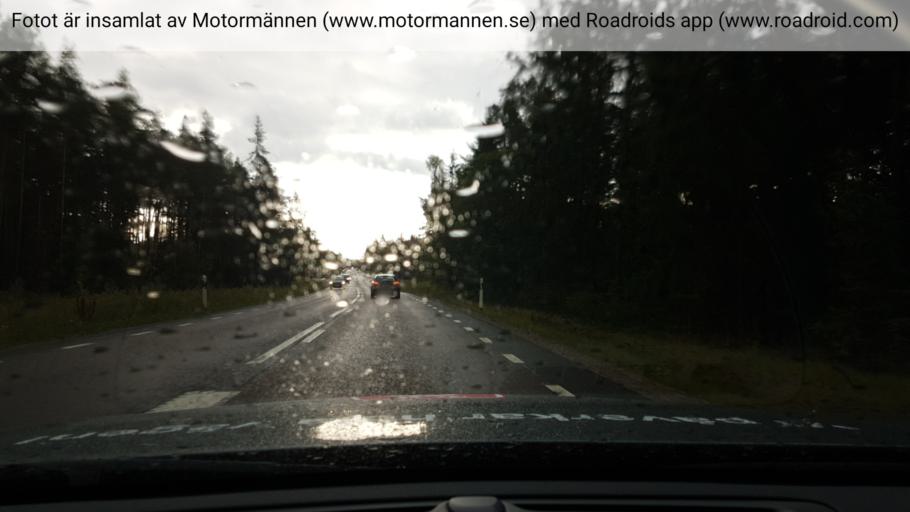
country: SE
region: Uppsala
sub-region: Alvkarleby Kommun
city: Skutskaer
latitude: 60.6499
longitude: 17.3477
